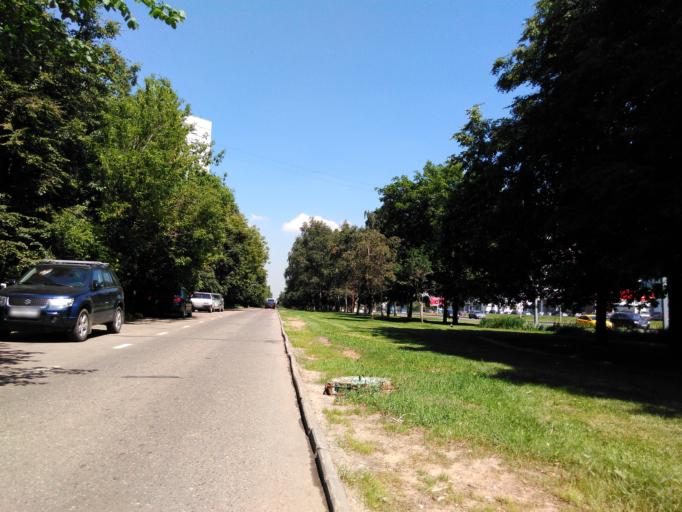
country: RU
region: Moscow
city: Troparevo
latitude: 55.6678
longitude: 37.5148
